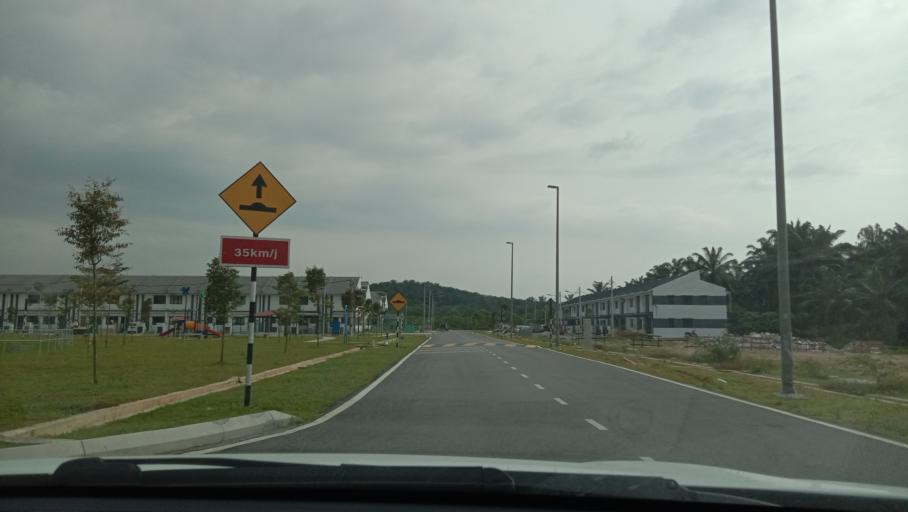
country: MY
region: Selangor
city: Ladang Seri Kundang
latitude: 3.2362
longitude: 101.4775
